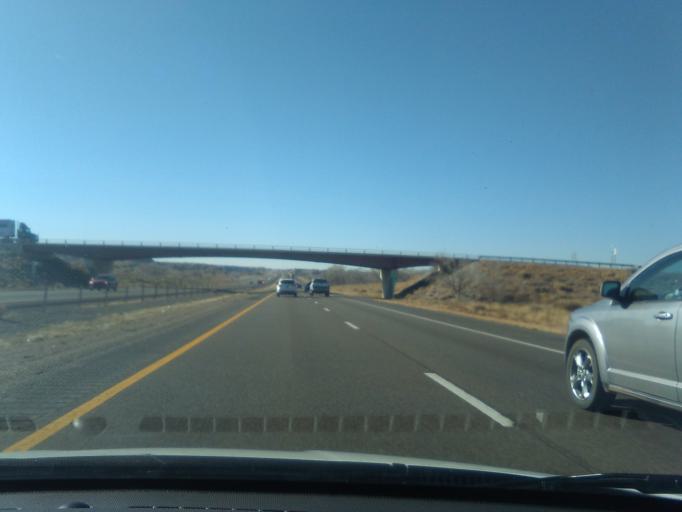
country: US
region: New Mexico
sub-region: Sandoval County
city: San Felipe Pueblo
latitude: 35.3796
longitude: -106.4682
